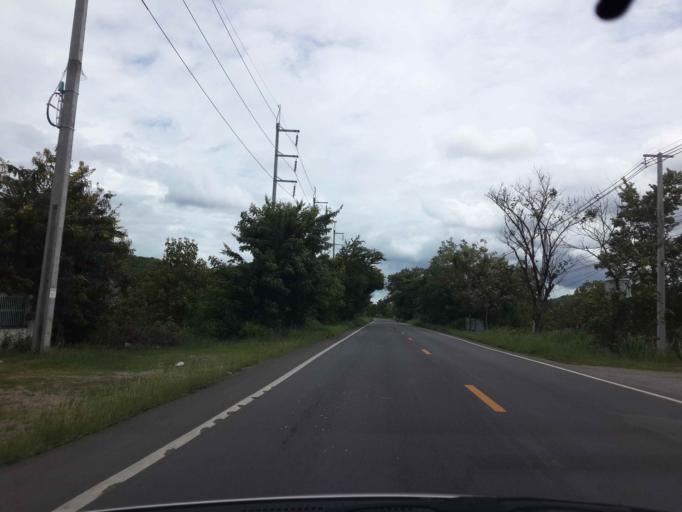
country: TH
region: Ratchaburi
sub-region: Amphoe Chom Bueng
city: Chom Bueng
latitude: 13.5488
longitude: 99.4781
